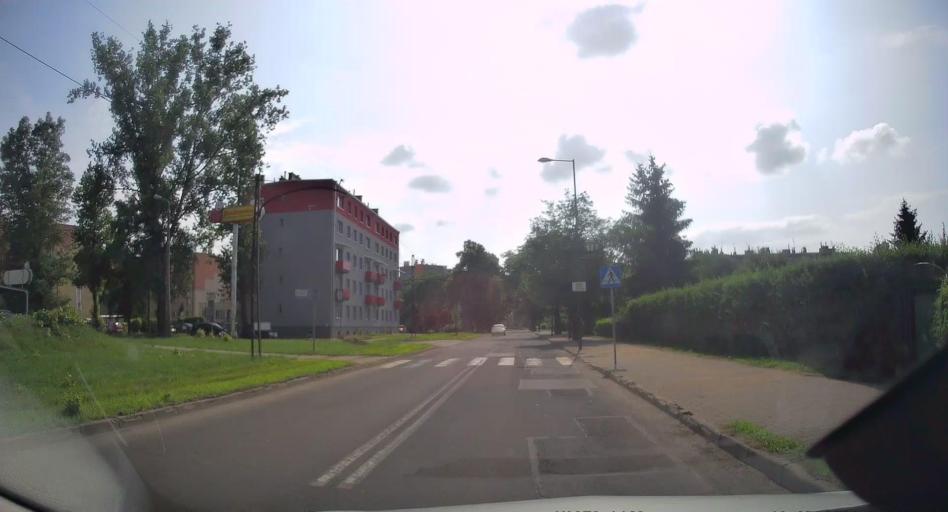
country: PL
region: Silesian Voivodeship
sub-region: Swietochlowice
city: Swietochlowice
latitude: 50.3174
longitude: 18.9188
